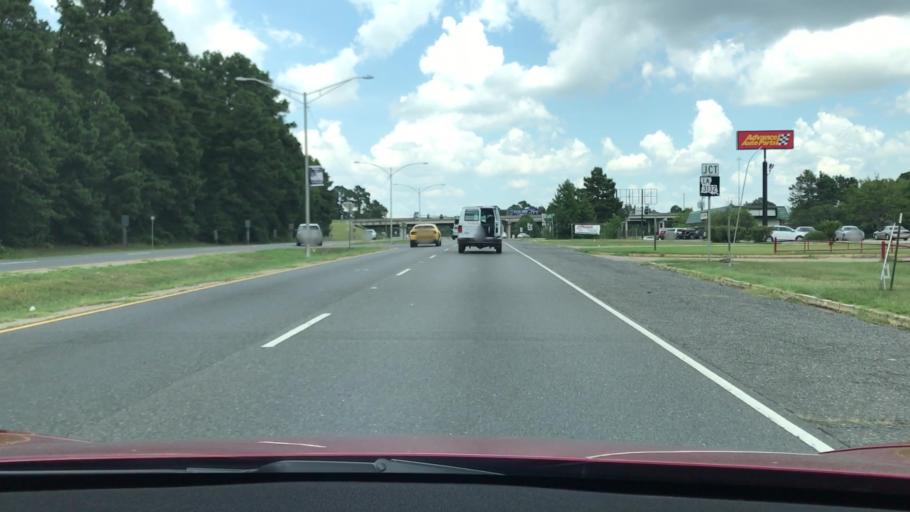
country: US
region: Louisiana
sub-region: Bossier Parish
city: Bossier City
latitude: 32.4136
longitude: -93.7923
